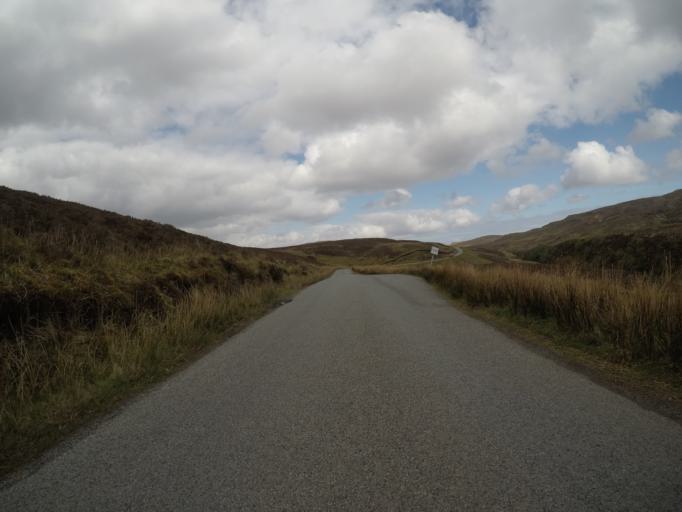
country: GB
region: Scotland
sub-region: Highland
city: Isle of Skye
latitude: 57.3798
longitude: -6.3644
